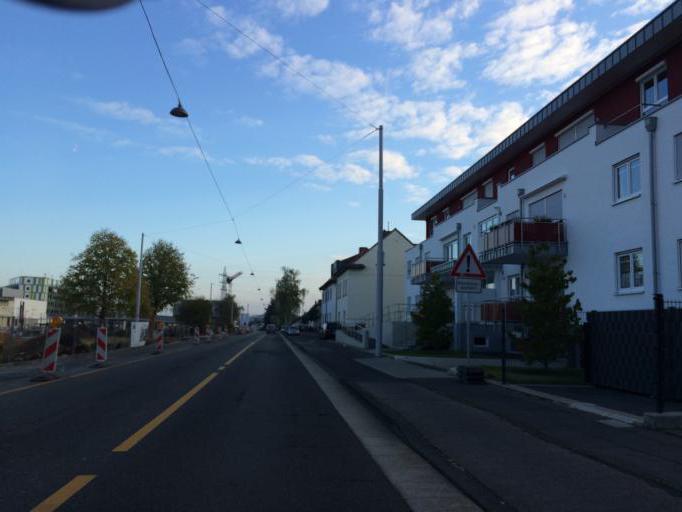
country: DE
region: North Rhine-Westphalia
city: Sankt Augustin
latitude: 50.7752
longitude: 7.1873
